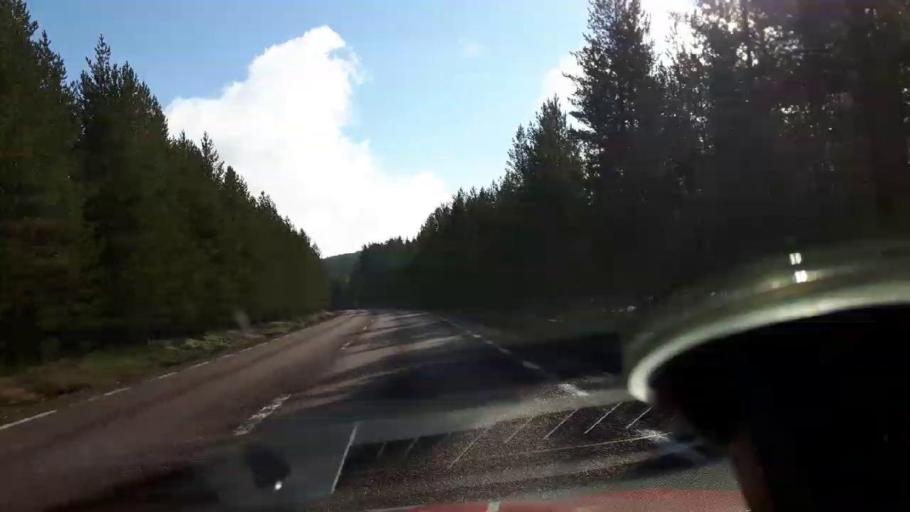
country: SE
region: Gaevleborg
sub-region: Ljusdals Kommun
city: Farila
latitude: 61.8903
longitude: 15.6681
